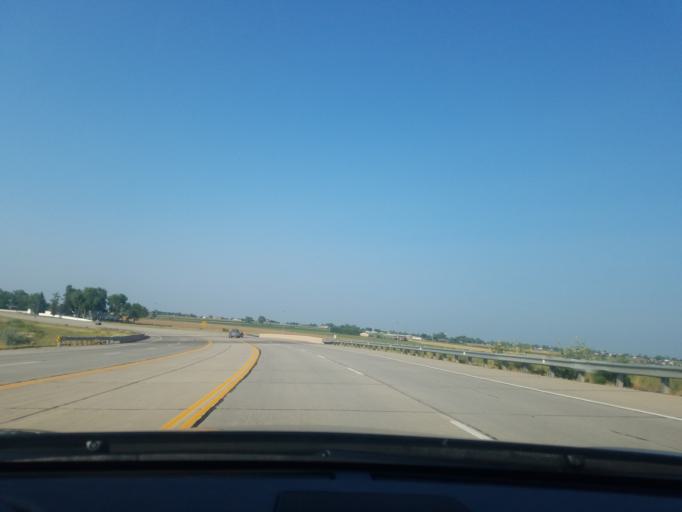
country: US
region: Colorado
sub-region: Larimer County
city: Campion
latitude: 40.3364
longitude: -105.0762
